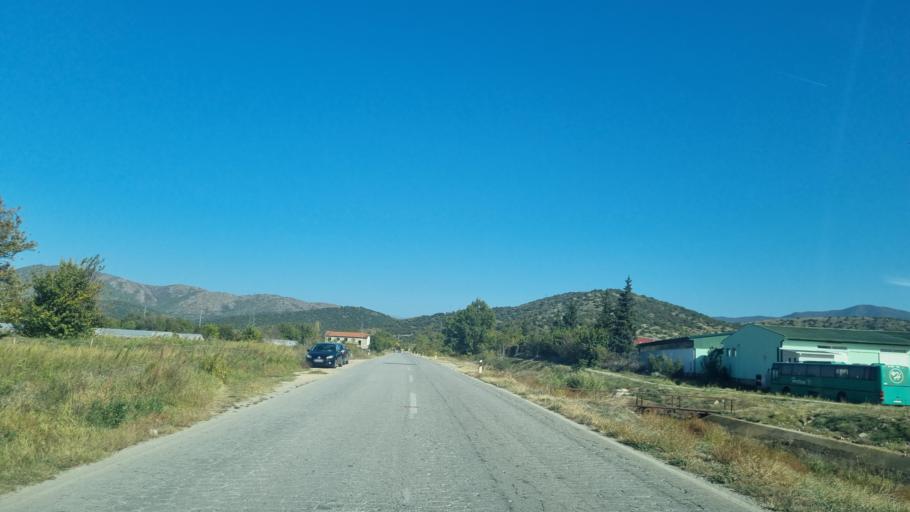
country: MK
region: Bogdanci
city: Bogdanci
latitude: 41.1968
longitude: 22.5833
